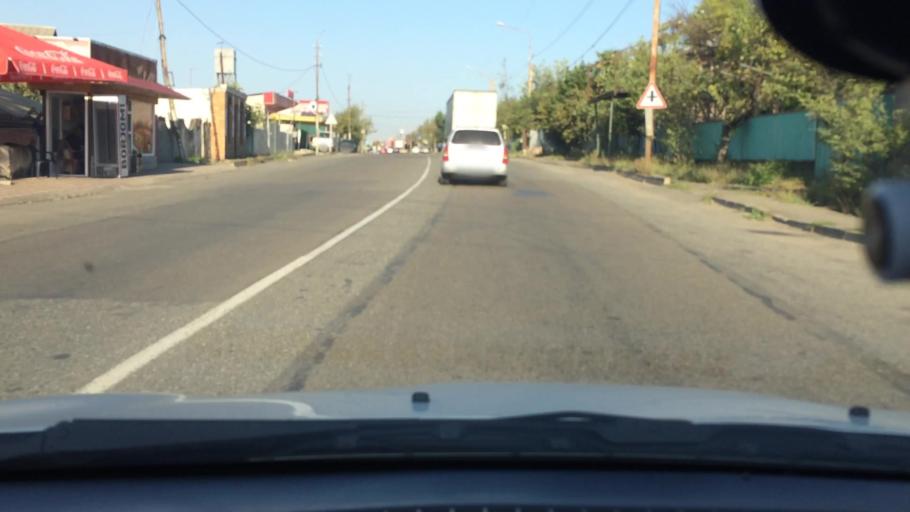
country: GE
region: Imereti
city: Zestap'oni
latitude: 42.1101
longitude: 43.0442
